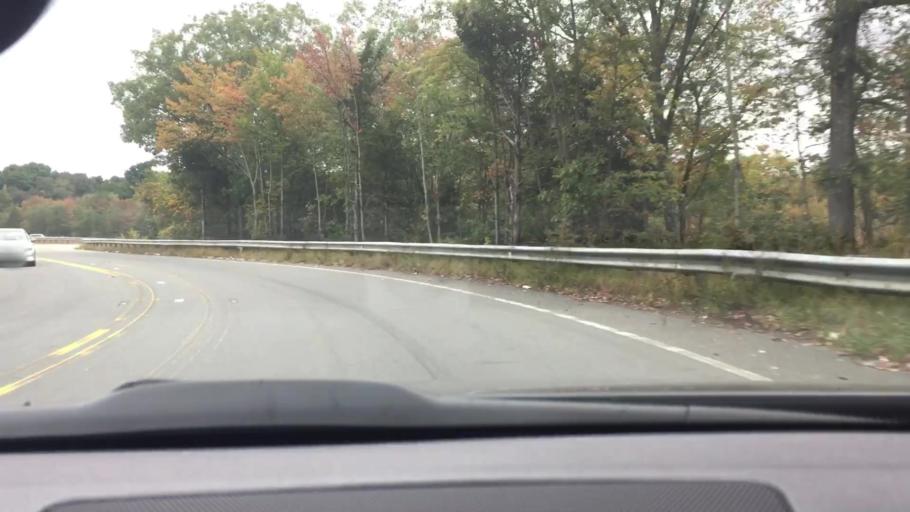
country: US
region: Massachusetts
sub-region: Norfolk County
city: Dedham
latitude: 42.2152
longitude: -71.1500
